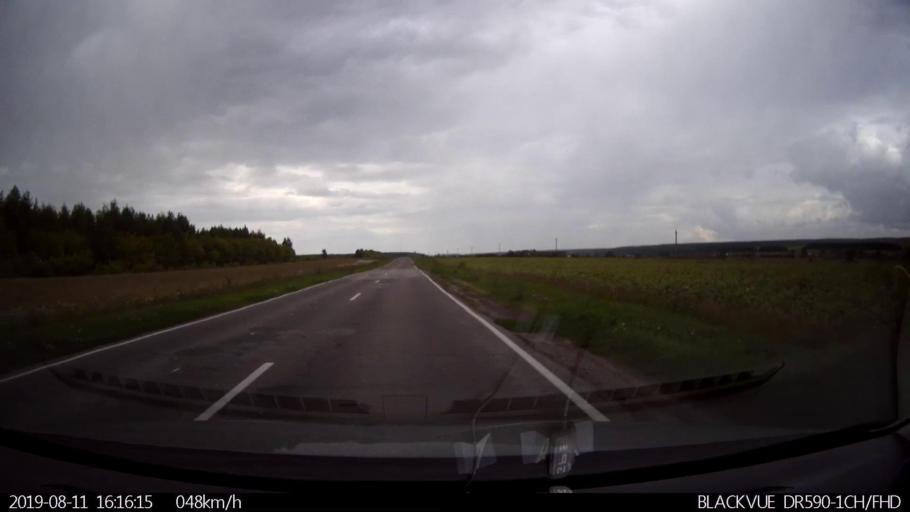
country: RU
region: Ulyanovsk
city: Mayna
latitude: 54.0396
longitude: 47.6223
